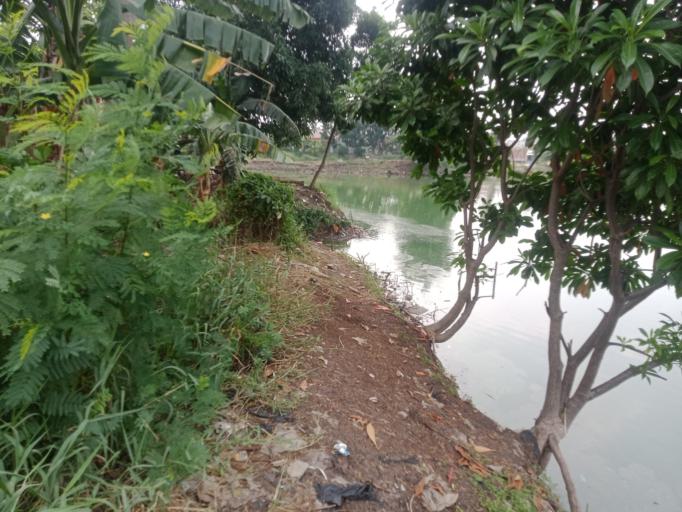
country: ID
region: West Java
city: Sepatan
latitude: -6.1607
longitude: 106.5813
